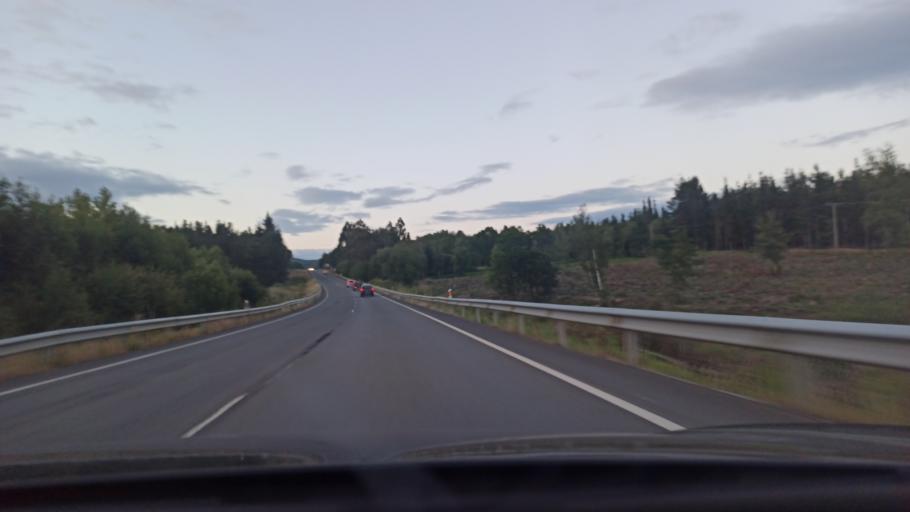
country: ES
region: Galicia
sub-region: Provincia de Lugo
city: Guntin
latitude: 42.9031
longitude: -7.6779
